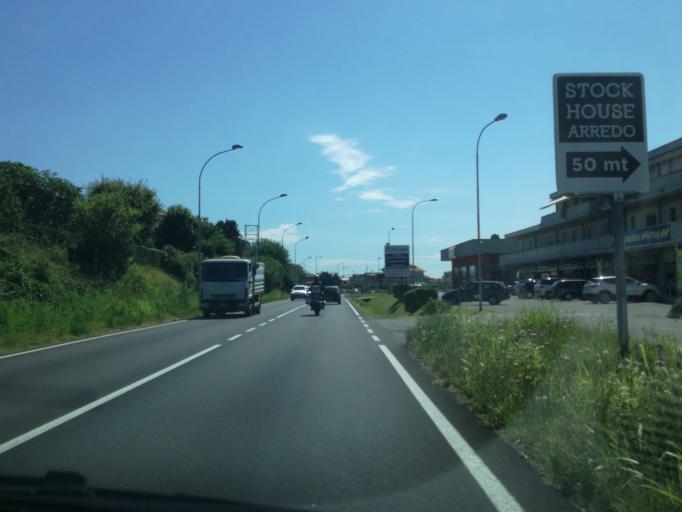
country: IT
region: Lombardy
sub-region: Provincia di Bergamo
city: Carvico
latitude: 45.7004
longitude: 9.4908
